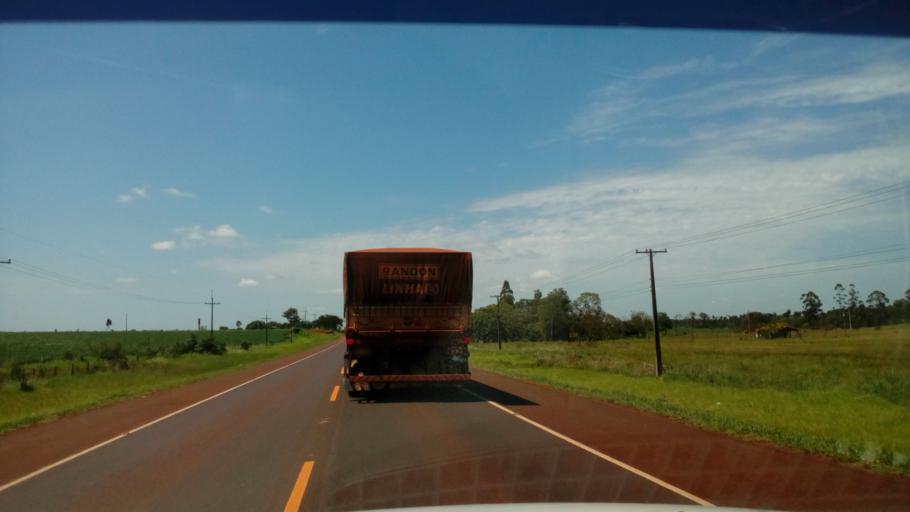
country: PY
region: Alto Parana
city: Colonia Yguazu
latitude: -25.5173
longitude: -54.8998
